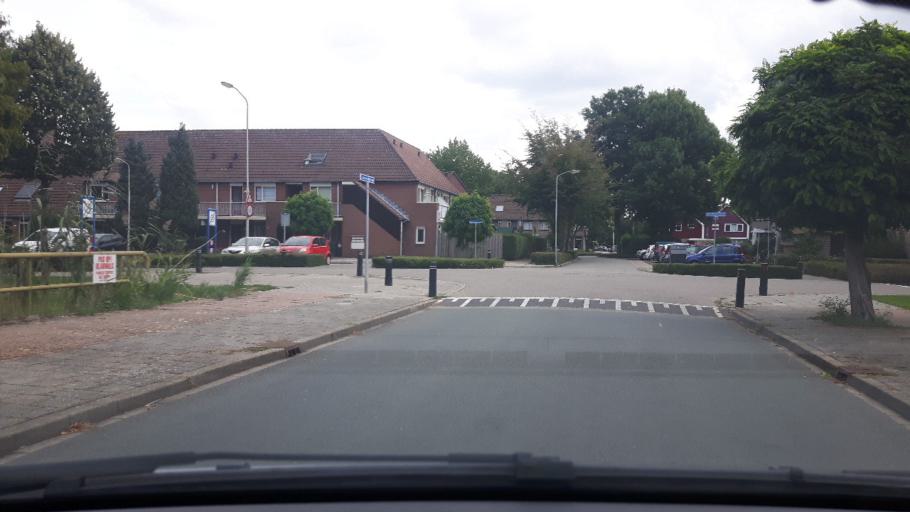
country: NL
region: Gelderland
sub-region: Gemeente Duiven
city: Duiven
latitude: 51.9521
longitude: 6.0094
